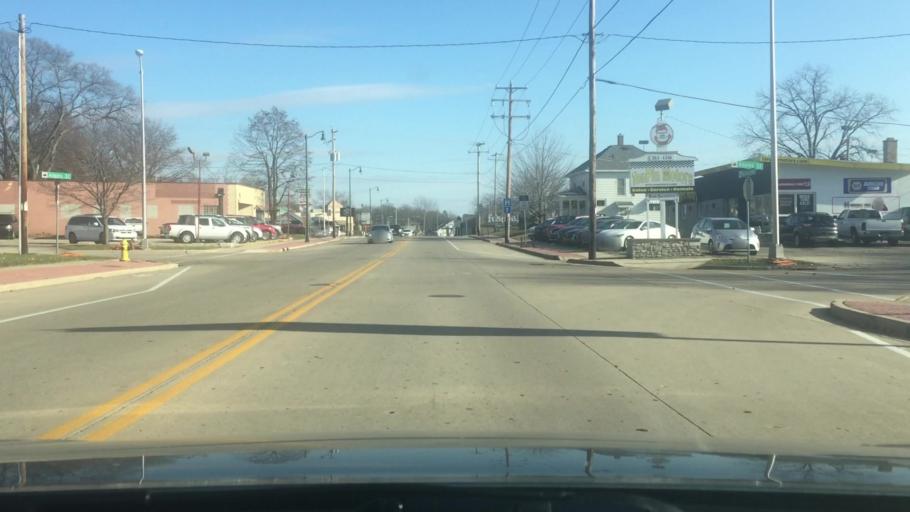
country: US
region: Wisconsin
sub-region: Jefferson County
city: Fort Atkinson
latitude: 42.9322
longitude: -88.8411
